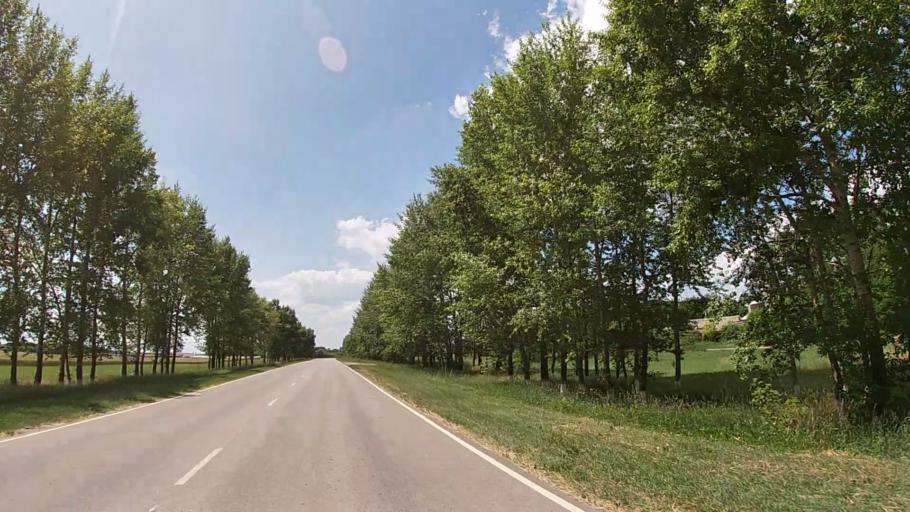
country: RU
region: Belgorod
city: Grayvoron
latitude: 50.4388
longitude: 35.6093
